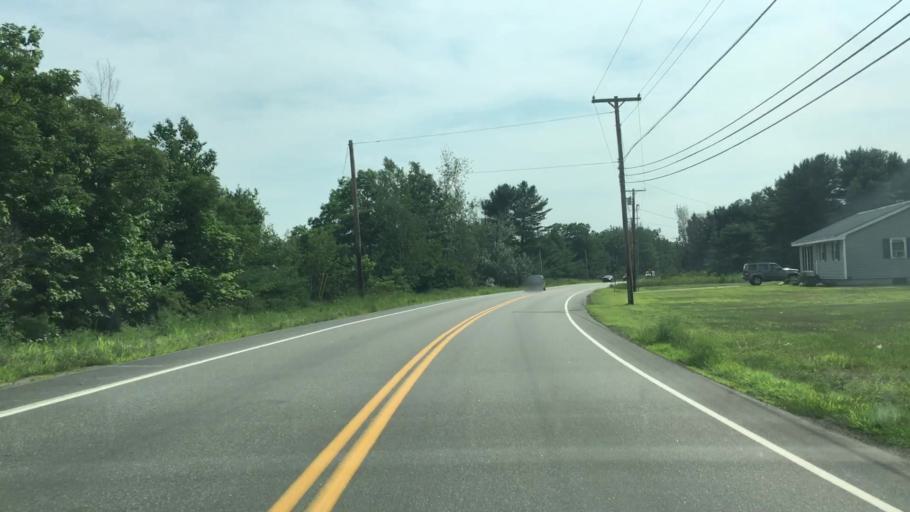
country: US
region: Maine
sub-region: Kennebec County
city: Windsor
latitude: 44.2925
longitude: -69.5859
